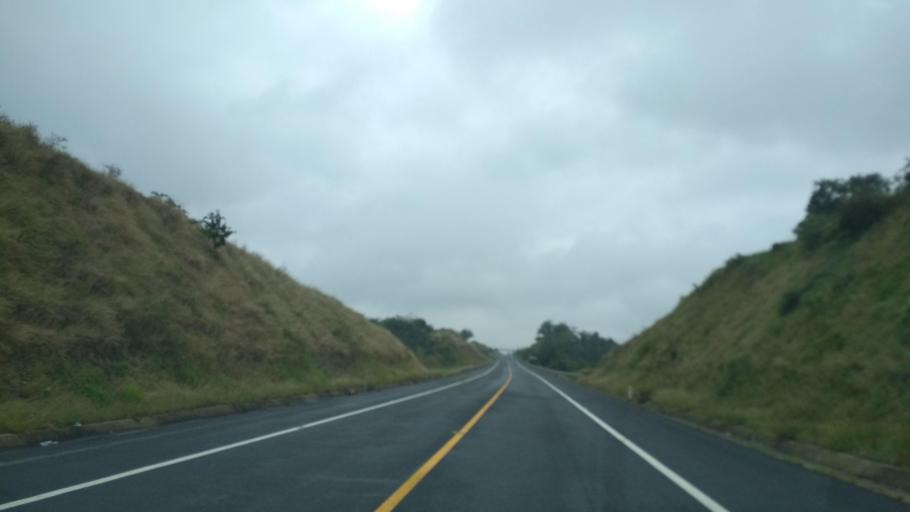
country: MX
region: Veracruz
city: Vega de San Marcos
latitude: 20.1787
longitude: -96.9642
